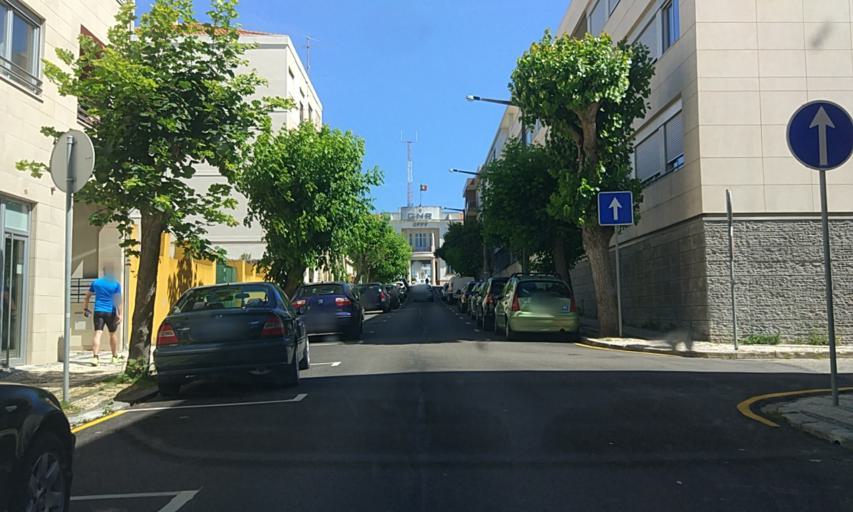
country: PT
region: Coimbra
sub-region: Figueira da Foz
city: Figueira da Foz
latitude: 40.1512
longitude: -8.8502
